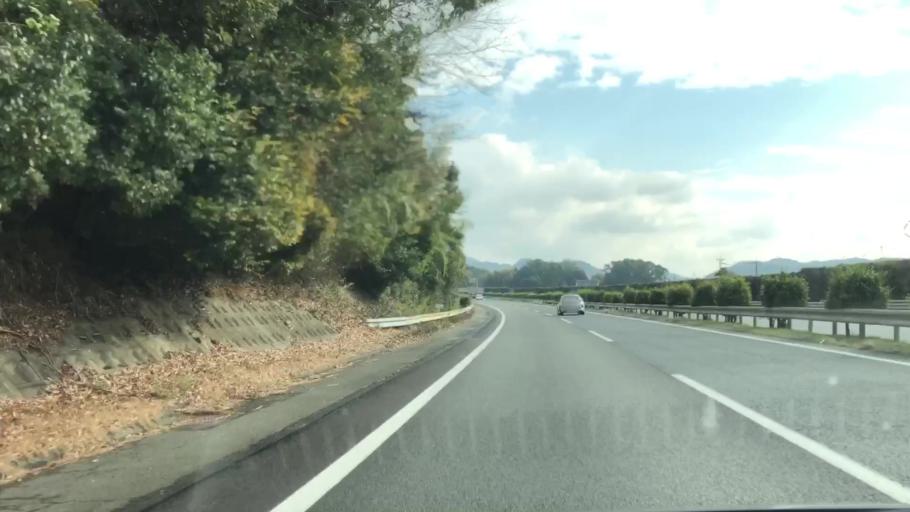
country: JP
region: Fukuoka
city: Setakamachi-takayanagi
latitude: 33.1217
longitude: 130.5207
